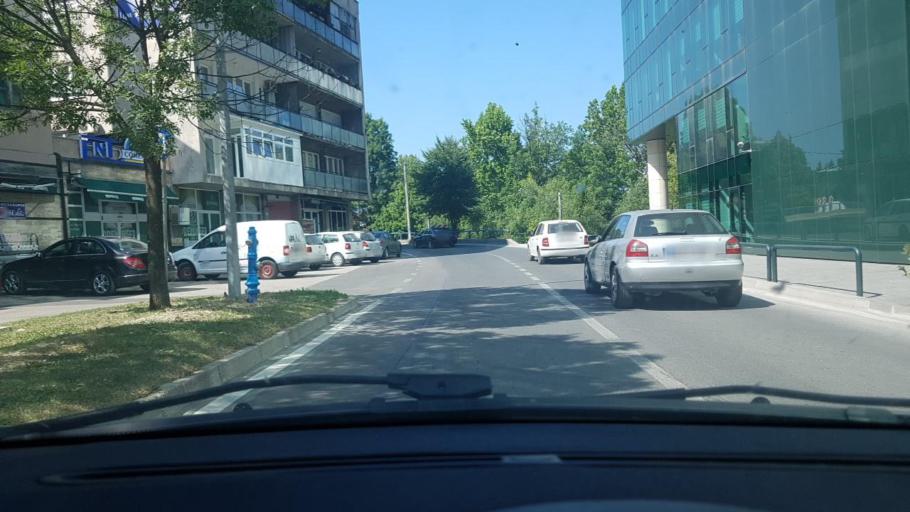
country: BA
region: Federation of Bosnia and Herzegovina
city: Bihac
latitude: 44.8157
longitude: 15.8706
